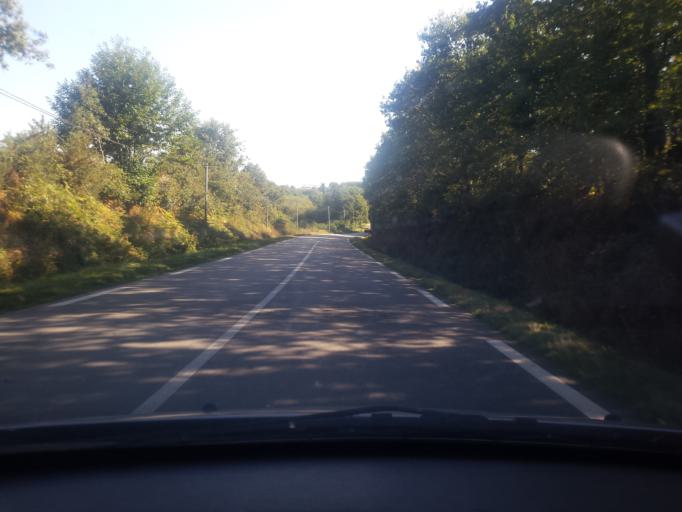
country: FR
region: Brittany
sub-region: Departement du Morbihan
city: Saint-Thuriau
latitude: 48.0424
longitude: -2.9251
